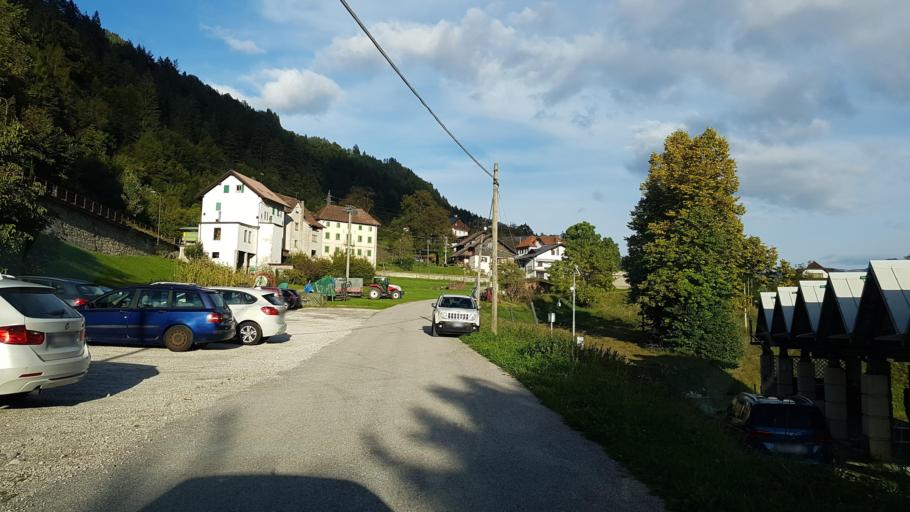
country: IT
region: Friuli Venezia Giulia
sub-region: Provincia di Udine
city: Pieria-Prato Carnico
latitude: 46.5218
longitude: 12.7747
